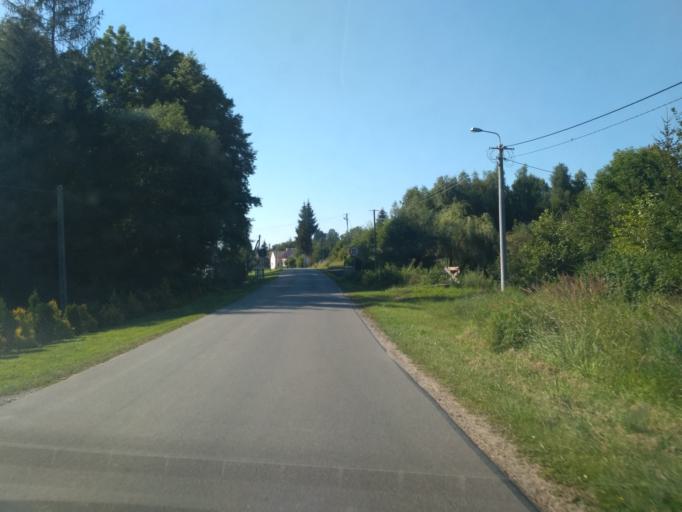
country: PL
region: Subcarpathian Voivodeship
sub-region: Powiat krosnienski
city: Odrzykon
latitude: 49.7746
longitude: 21.7801
